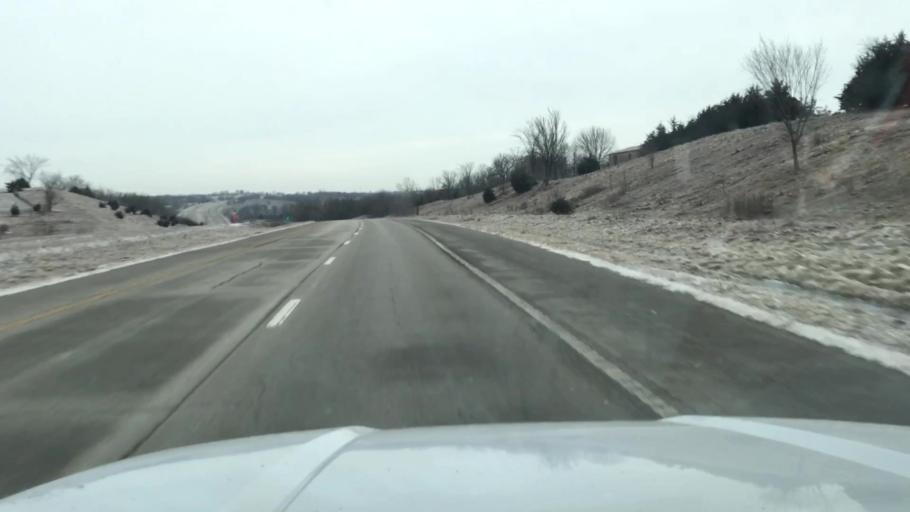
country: US
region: Missouri
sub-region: Andrew County
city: Savannah
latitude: 39.8997
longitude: -94.8570
